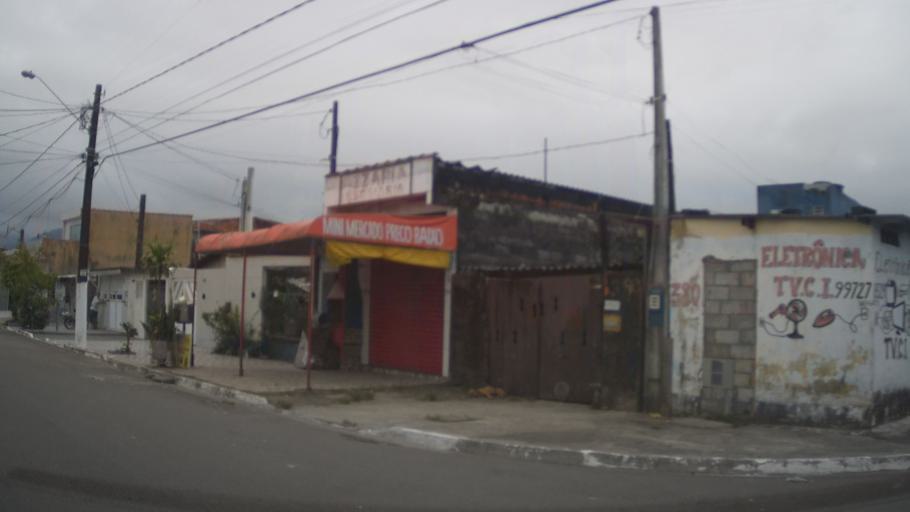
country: BR
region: Sao Paulo
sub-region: Praia Grande
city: Praia Grande
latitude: -24.0215
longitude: -46.4914
